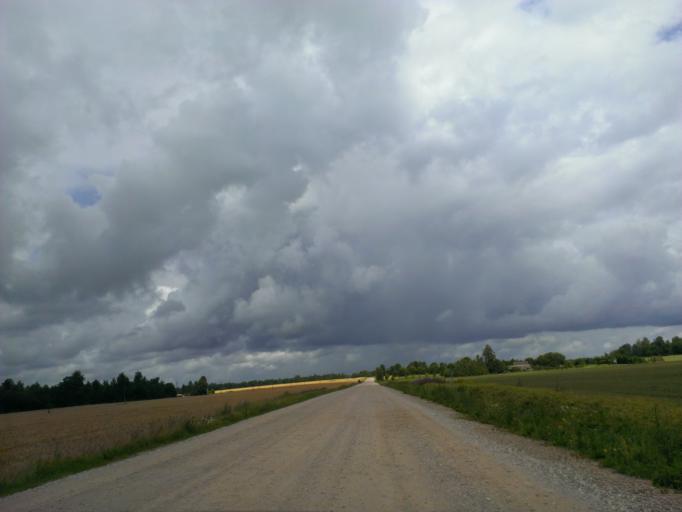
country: LV
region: Sigulda
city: Sigulda
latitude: 57.1862
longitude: 24.9384
